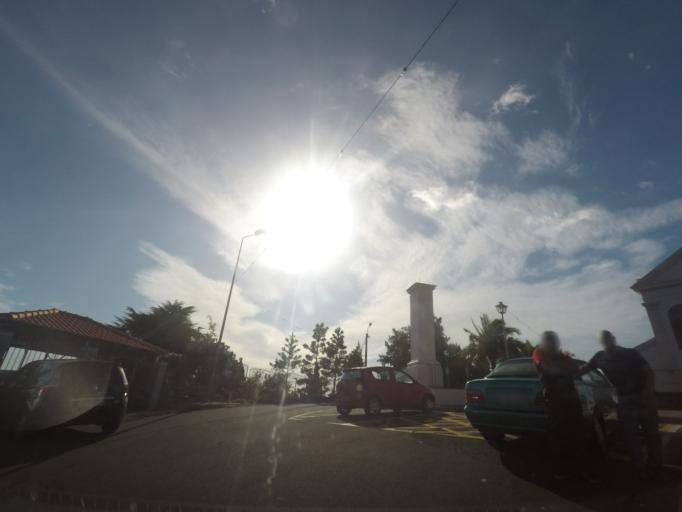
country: PT
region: Madeira
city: Camara de Lobos
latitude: 32.6493
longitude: -16.9431
